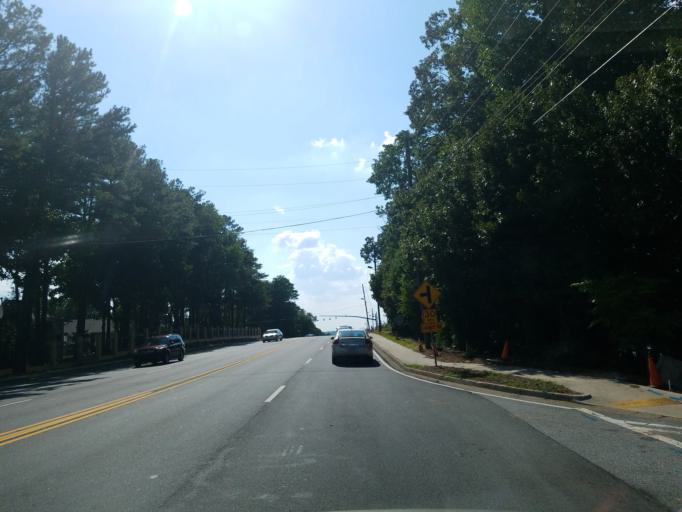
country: US
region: Georgia
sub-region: DeKalb County
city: Dunwoody
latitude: 33.9820
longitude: -84.3457
